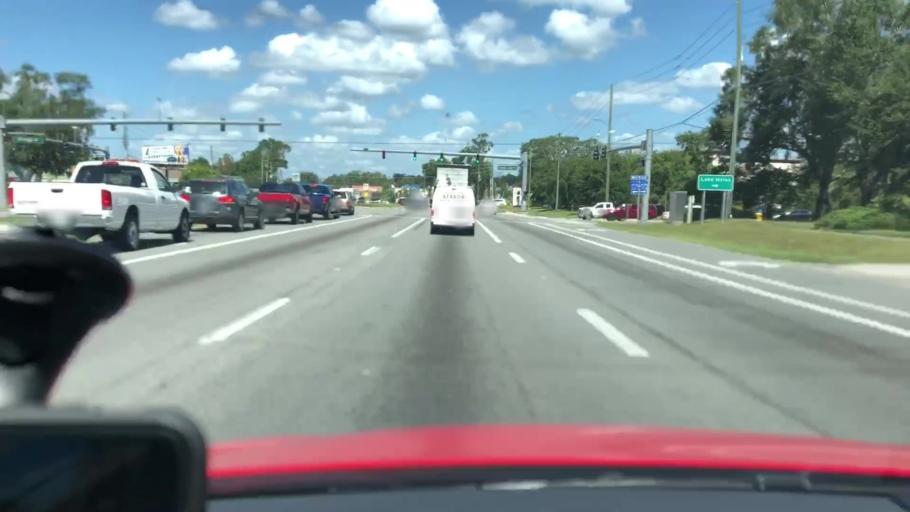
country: US
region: Florida
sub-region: Volusia County
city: De Land Southwest
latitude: 28.9837
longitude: -81.2993
